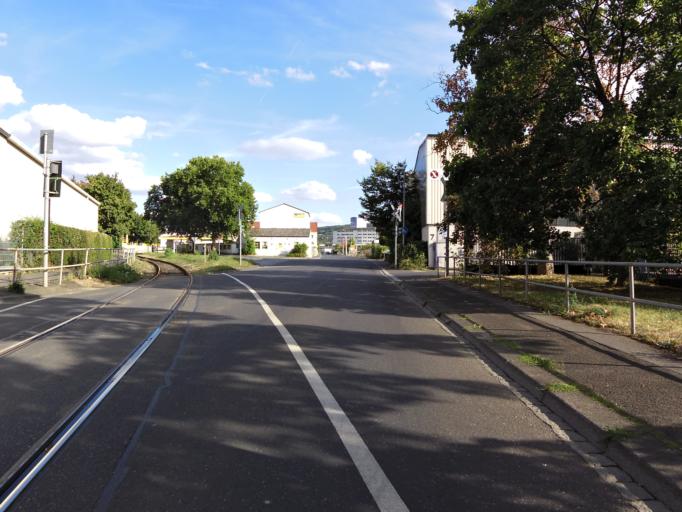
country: DE
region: Bavaria
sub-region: Regierungsbezirk Unterfranken
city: Zell am Main
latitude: 49.8046
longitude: 9.8815
